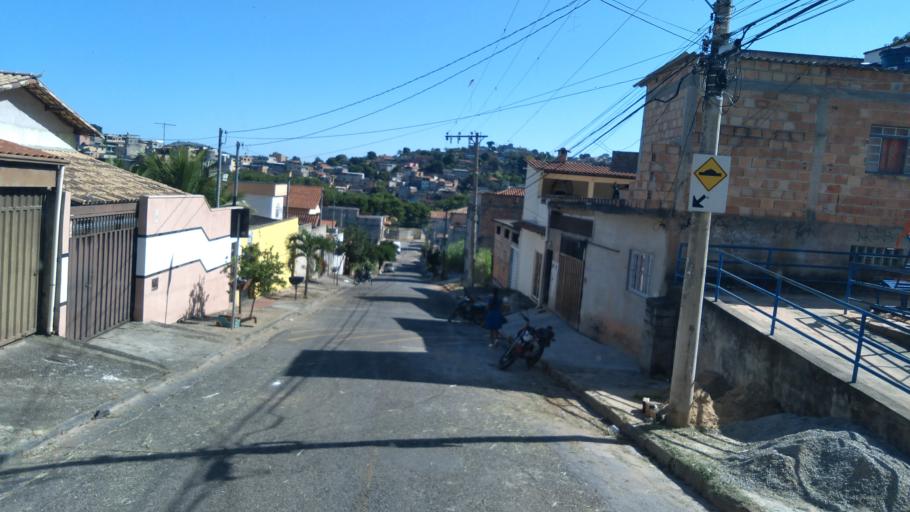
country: BR
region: Minas Gerais
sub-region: Belo Horizonte
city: Belo Horizonte
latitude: -19.8453
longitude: -43.9068
